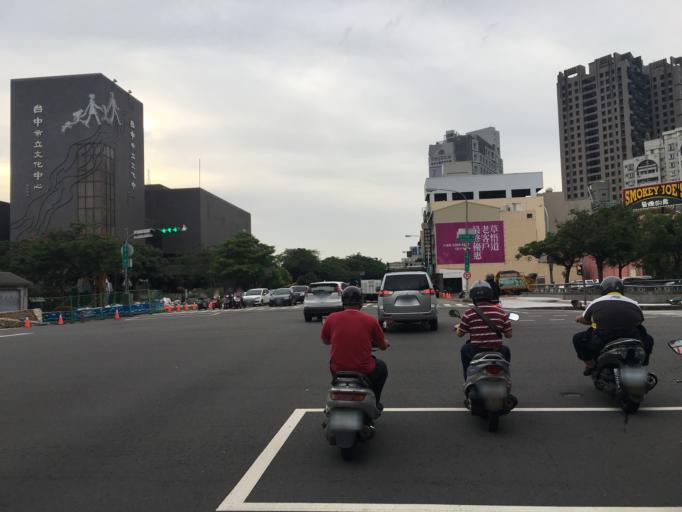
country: TW
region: Taiwan
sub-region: Taichung City
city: Taichung
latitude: 24.1412
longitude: 120.6670
